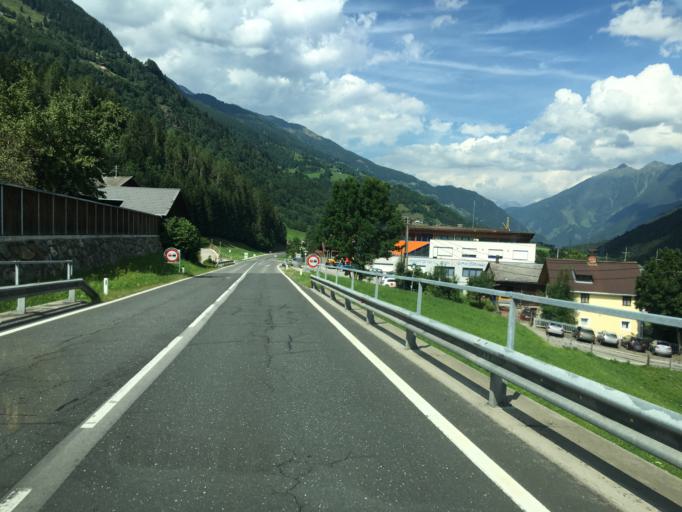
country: AT
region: Carinthia
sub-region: Politischer Bezirk Spittal an der Drau
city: Rangersdorf
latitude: 46.8640
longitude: 12.9683
